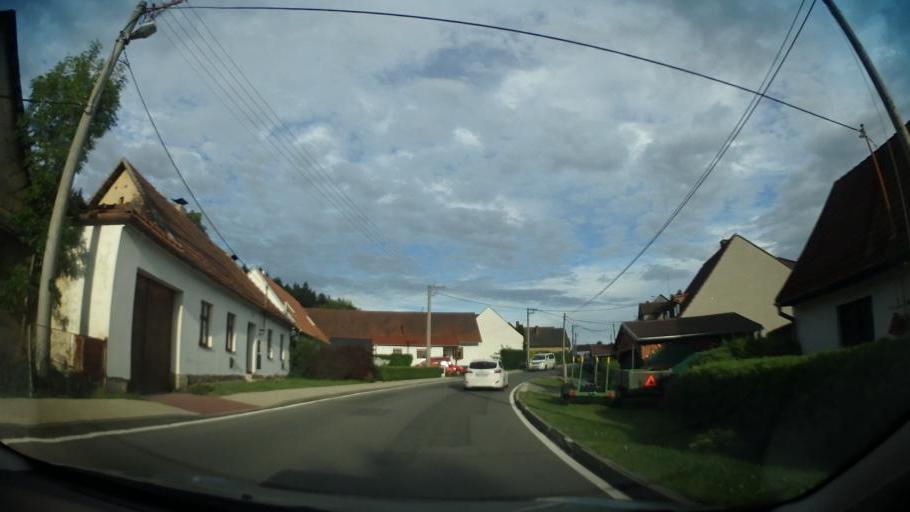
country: CZ
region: Olomoucky
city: Horni Stepanov
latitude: 49.5614
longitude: 16.7569
